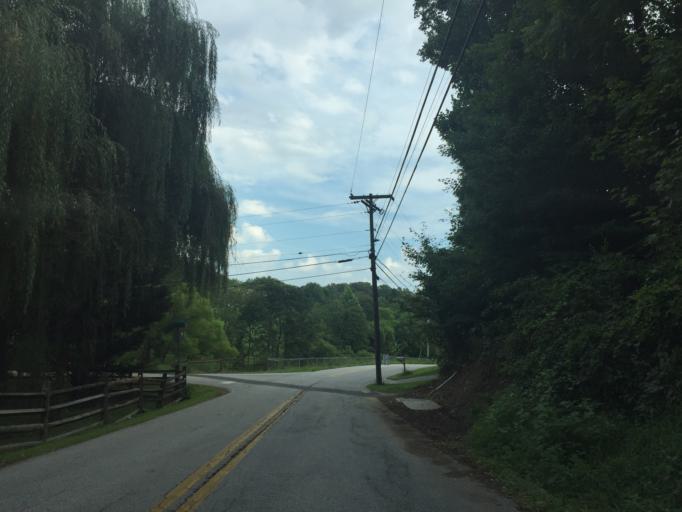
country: US
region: Maryland
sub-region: Carroll County
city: Manchester
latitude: 39.6223
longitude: -76.9019
